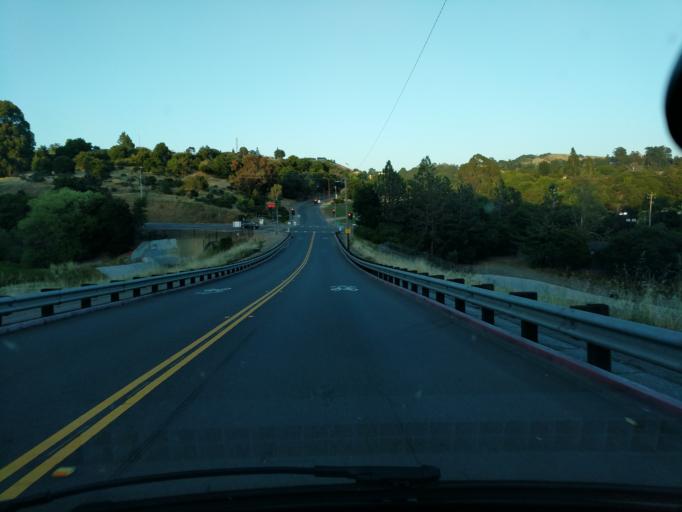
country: US
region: California
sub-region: Alameda County
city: Fairview
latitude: 37.7038
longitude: -122.0565
